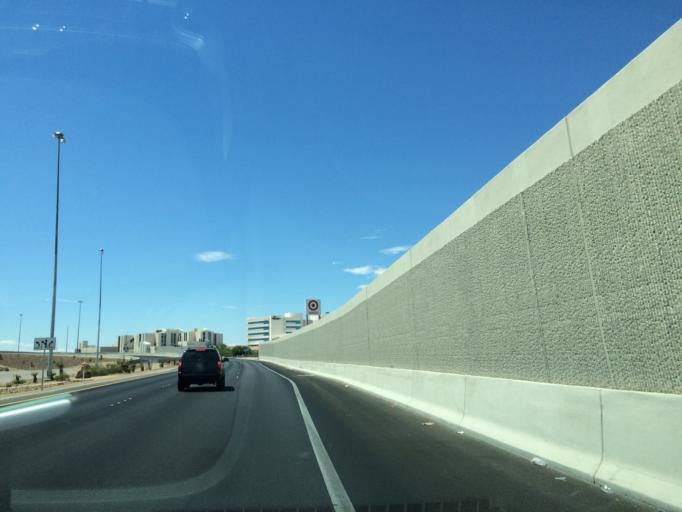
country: US
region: Nevada
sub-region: Clark County
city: Spring Valley
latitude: 36.2206
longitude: -115.2477
